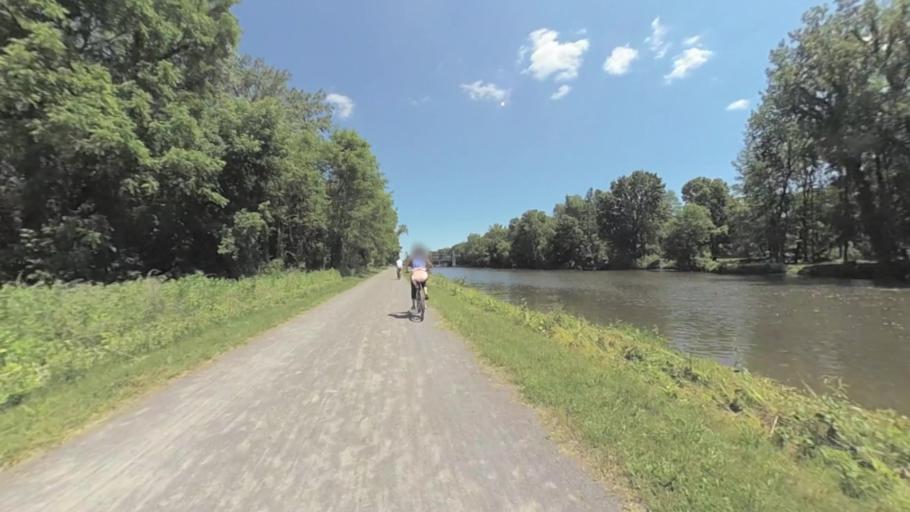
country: US
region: New York
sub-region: Monroe County
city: Fairport
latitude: 43.0669
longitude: -77.4700
